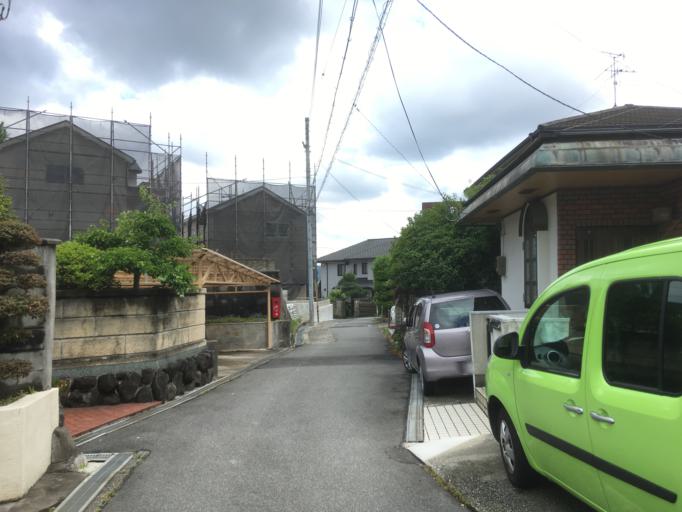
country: JP
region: Nara
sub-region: Ikoma-shi
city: Ikoma
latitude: 34.6876
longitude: 135.6982
